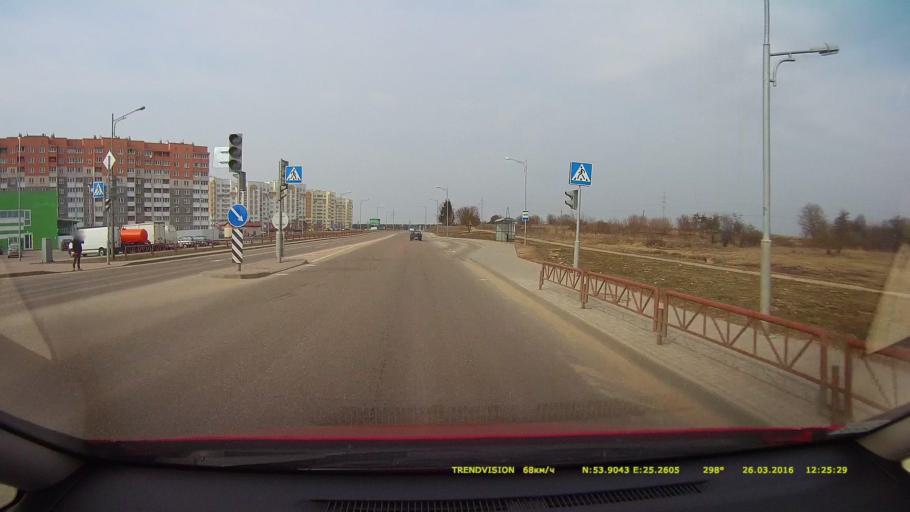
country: BY
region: Grodnenskaya
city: Lida
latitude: 53.9043
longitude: 25.2604
